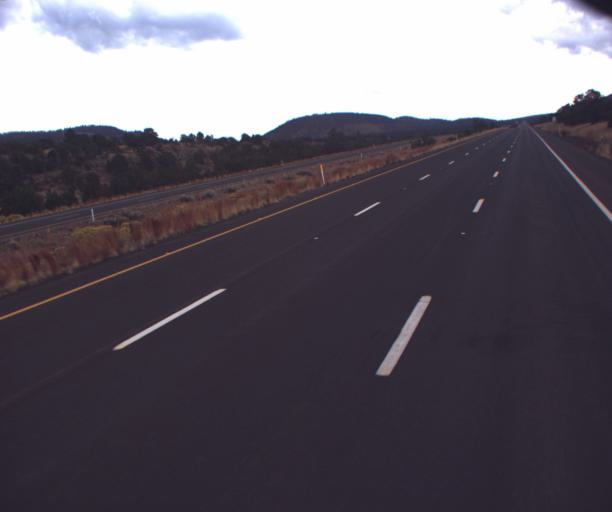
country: US
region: Arizona
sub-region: Coconino County
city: Flagstaff
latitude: 35.4210
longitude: -111.5710
